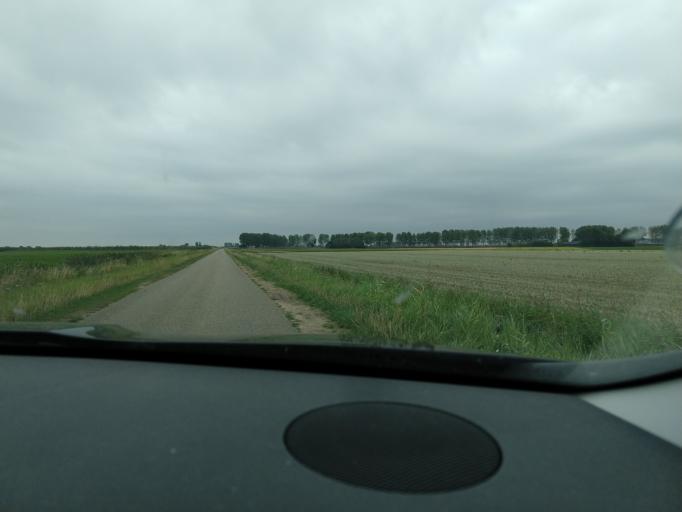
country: NL
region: Zeeland
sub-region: Gemeente Hulst
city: Hulst
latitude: 51.3451
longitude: 4.0729
